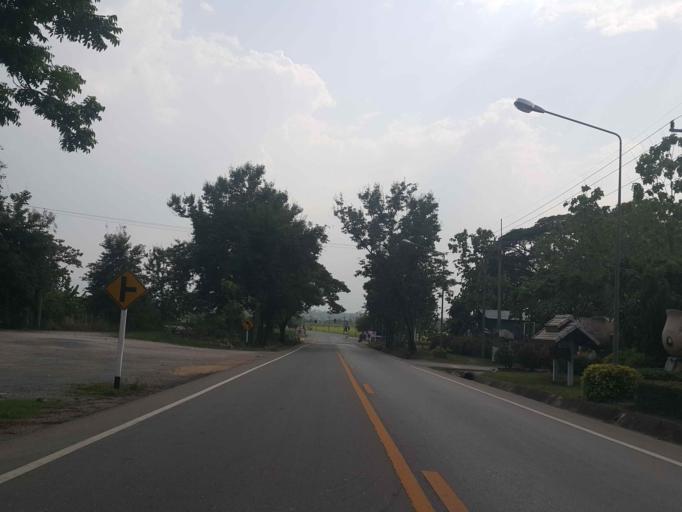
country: TH
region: Chiang Mai
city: Mae Taeng
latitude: 19.0675
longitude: 98.9624
